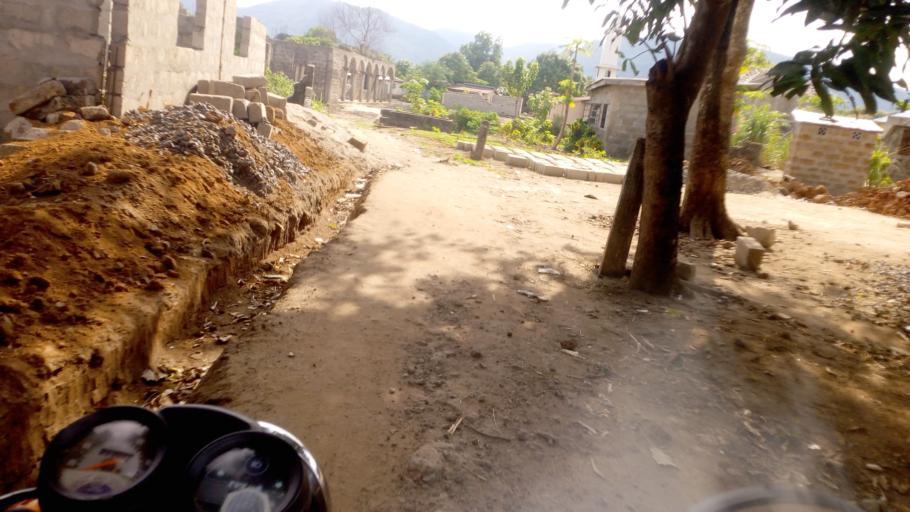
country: SL
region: Western Area
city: Waterloo
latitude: 8.3220
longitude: -13.0767
